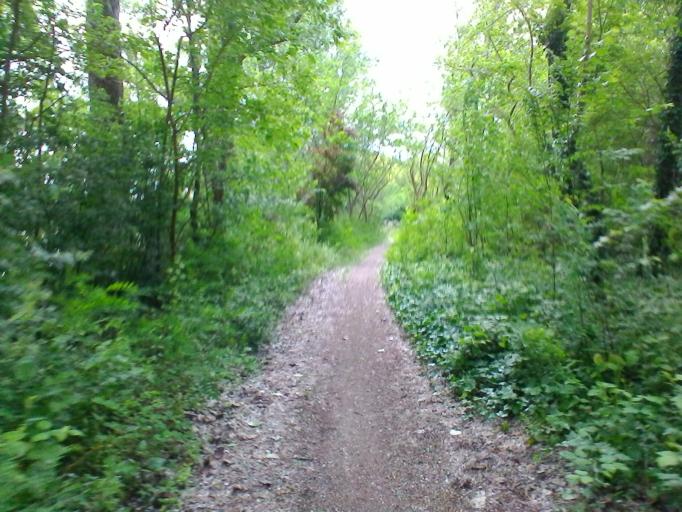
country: IT
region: Lombardy
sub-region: Provincia di Mantova
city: Cerese
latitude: 45.1316
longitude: 10.8139
